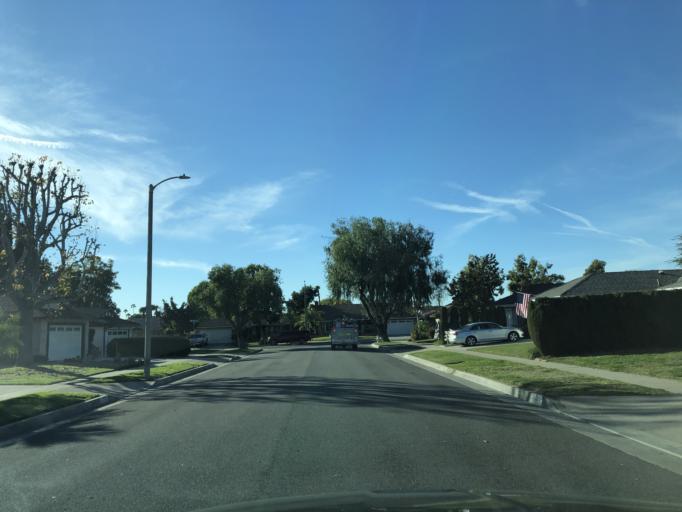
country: US
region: California
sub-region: Orange County
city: Tustin
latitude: 33.7632
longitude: -117.8375
